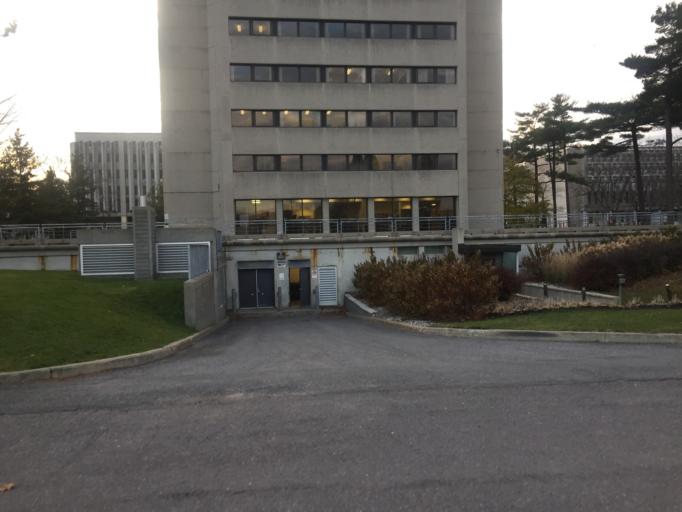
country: CA
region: Quebec
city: Quebec
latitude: 46.7812
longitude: -71.2721
